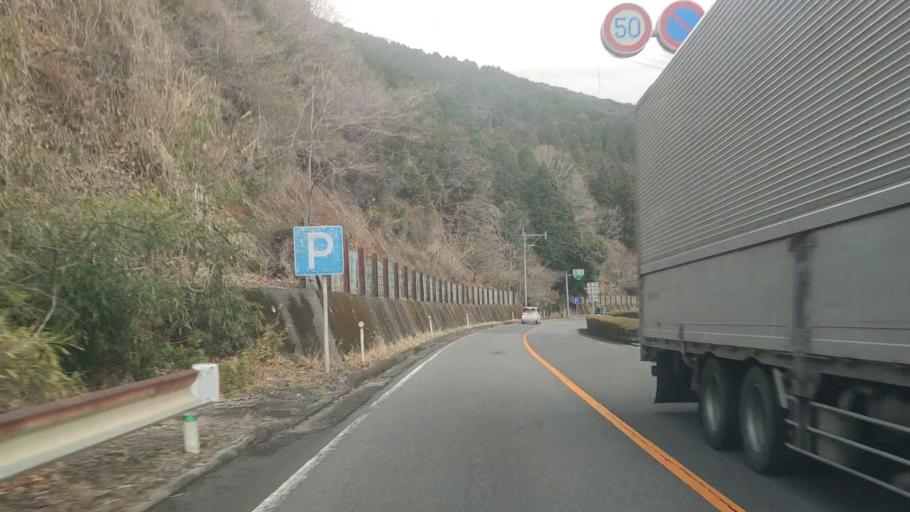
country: JP
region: Kumamoto
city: Hitoyoshi
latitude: 32.0715
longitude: 130.8013
